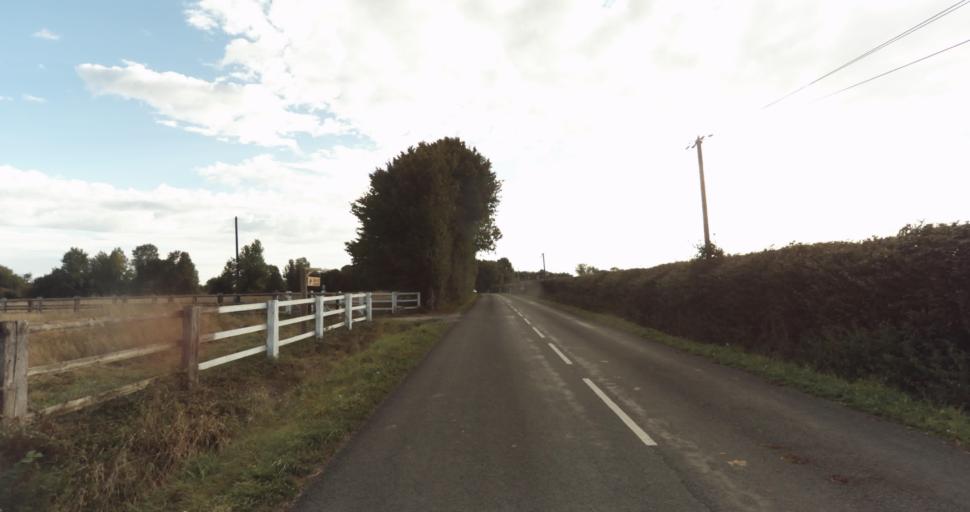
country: FR
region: Lower Normandy
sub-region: Departement de l'Orne
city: Vimoutiers
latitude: 48.9471
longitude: 0.2479
